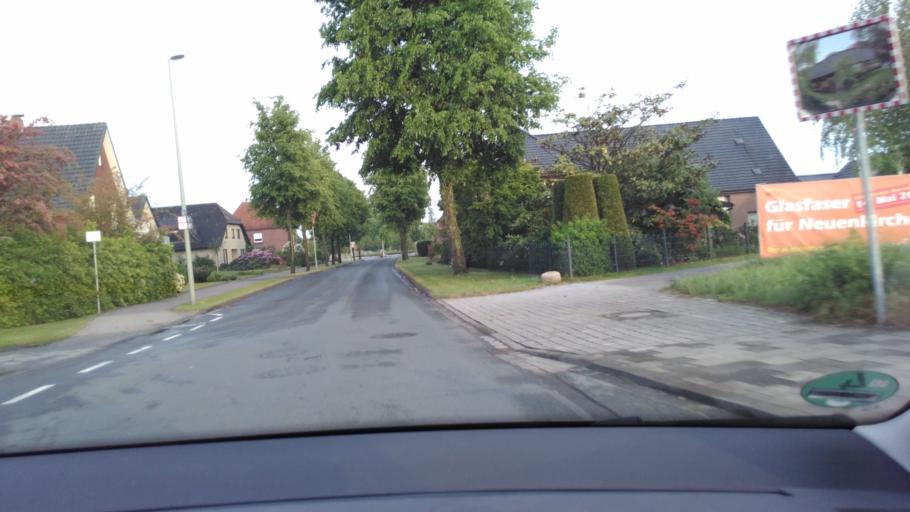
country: DE
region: North Rhine-Westphalia
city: Rietberg
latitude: 51.8280
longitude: 8.4475
